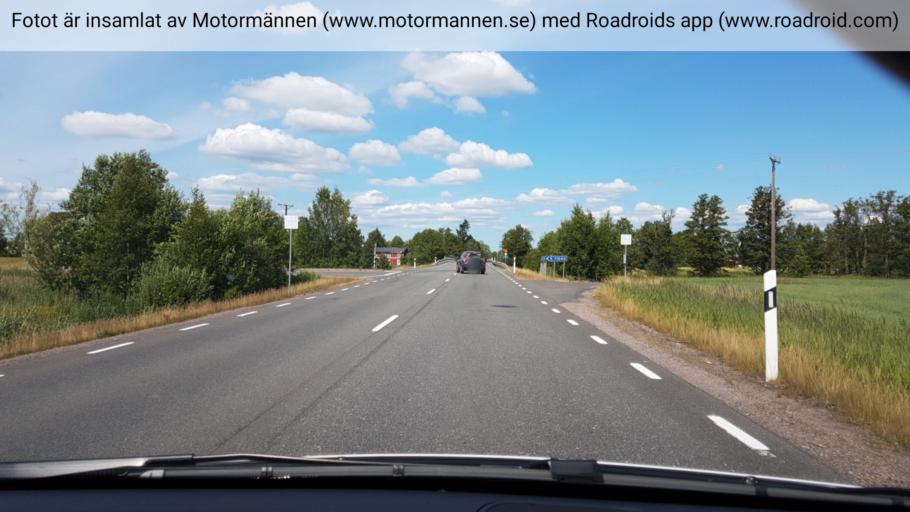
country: SE
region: Vaestra Goetaland
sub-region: Toreboda Kommun
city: Toereboda
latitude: 58.5751
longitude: 14.0988
